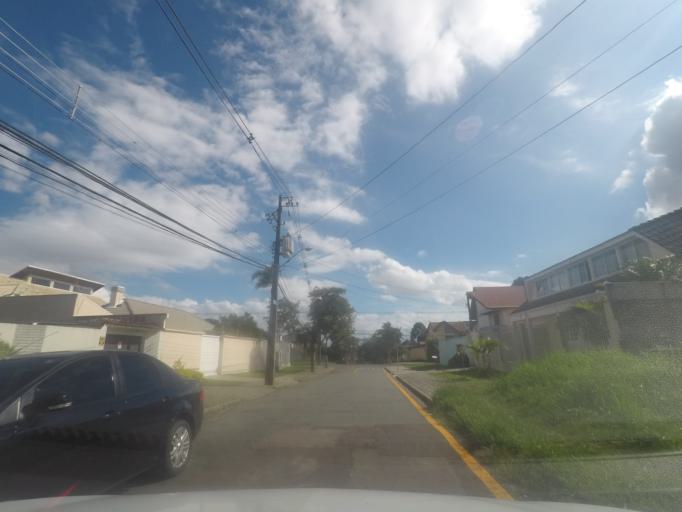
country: BR
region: Parana
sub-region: Pinhais
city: Pinhais
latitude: -25.4629
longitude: -49.2243
